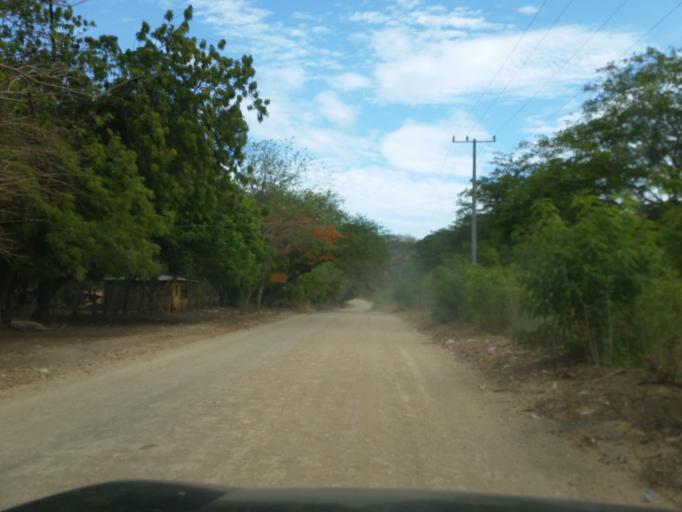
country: NI
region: Rivas
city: Tola
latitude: 11.4155
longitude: -86.0089
